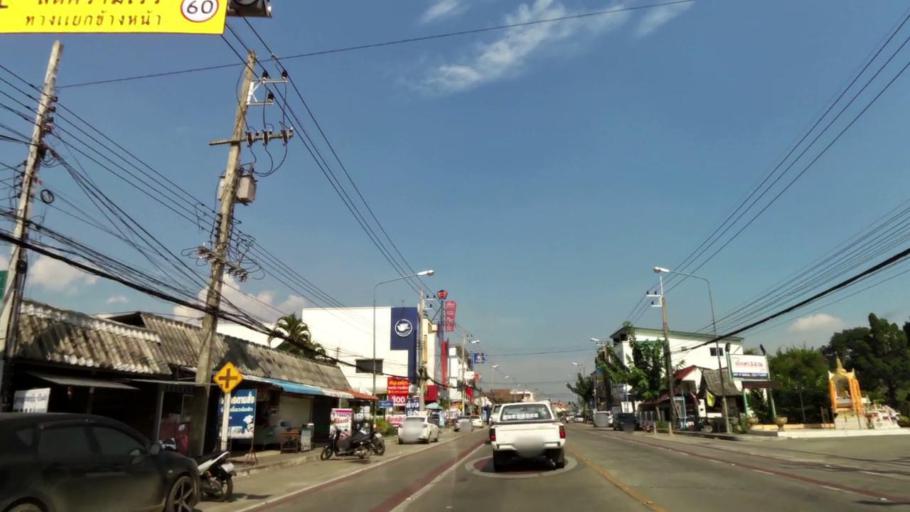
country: TH
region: Chiang Rai
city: Chiang Rai
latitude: 19.9242
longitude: 99.8352
